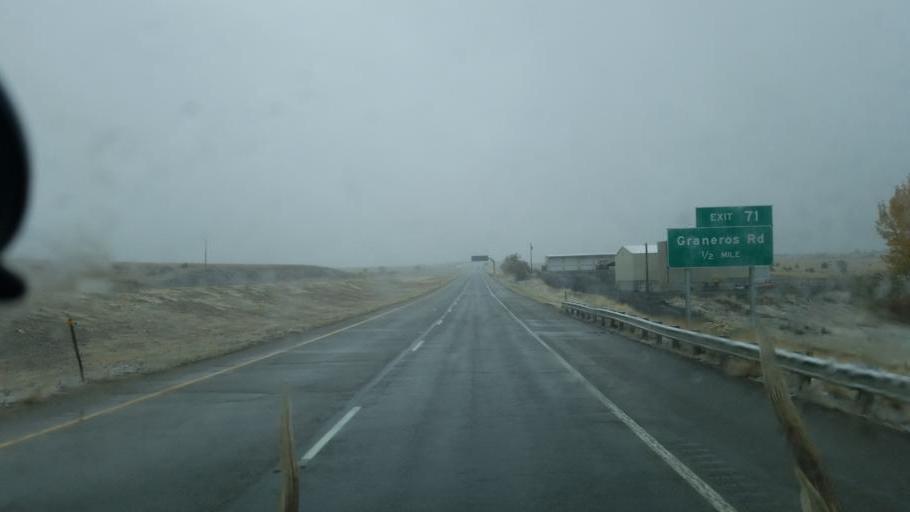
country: US
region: Colorado
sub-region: Pueblo County
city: Colorado City
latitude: 37.9138
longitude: -104.8273
